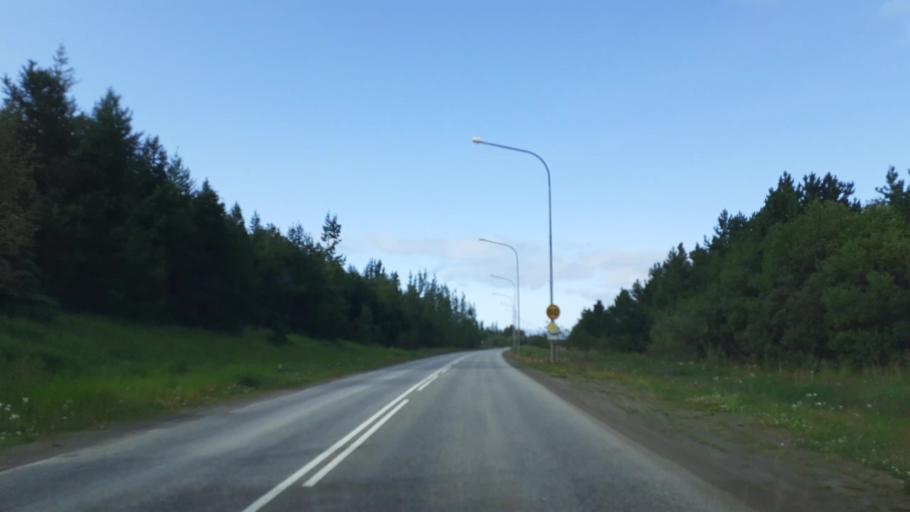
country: IS
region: Northeast
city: Akureyri
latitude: 65.6550
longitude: -18.0798
